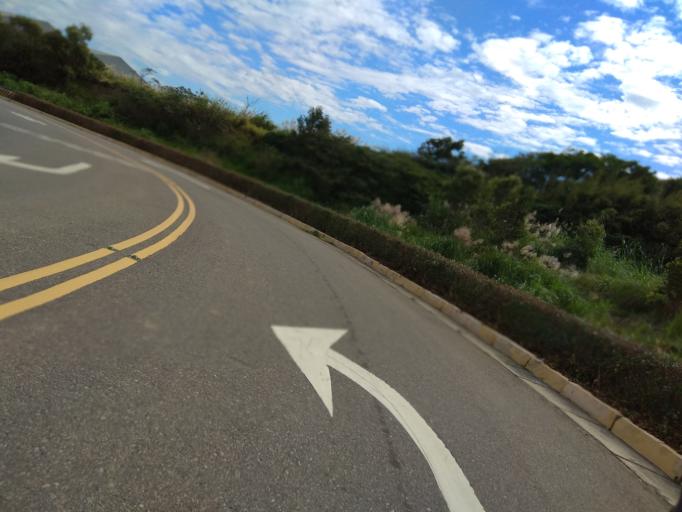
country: TW
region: Taiwan
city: Taoyuan City
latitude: 25.0491
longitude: 121.0910
